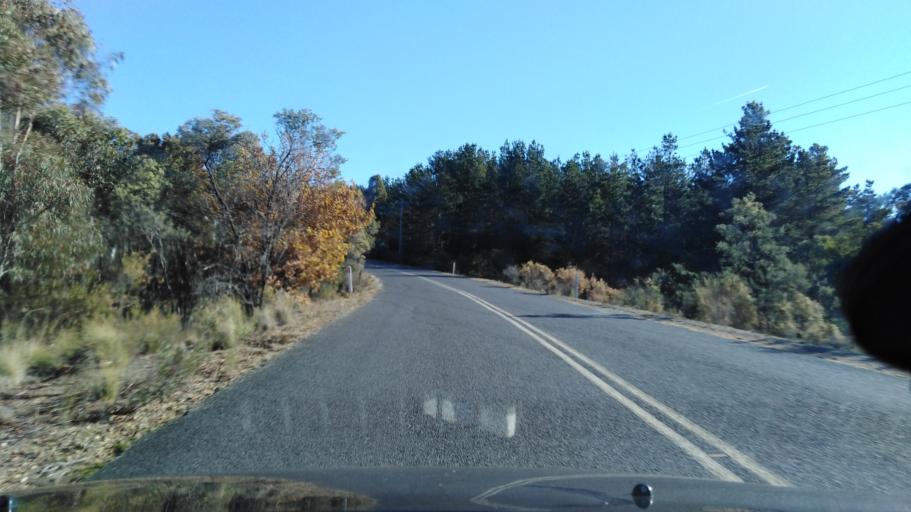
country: AU
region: New South Wales
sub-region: Palerang
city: Bungendore
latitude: -35.2090
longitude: 149.3398
